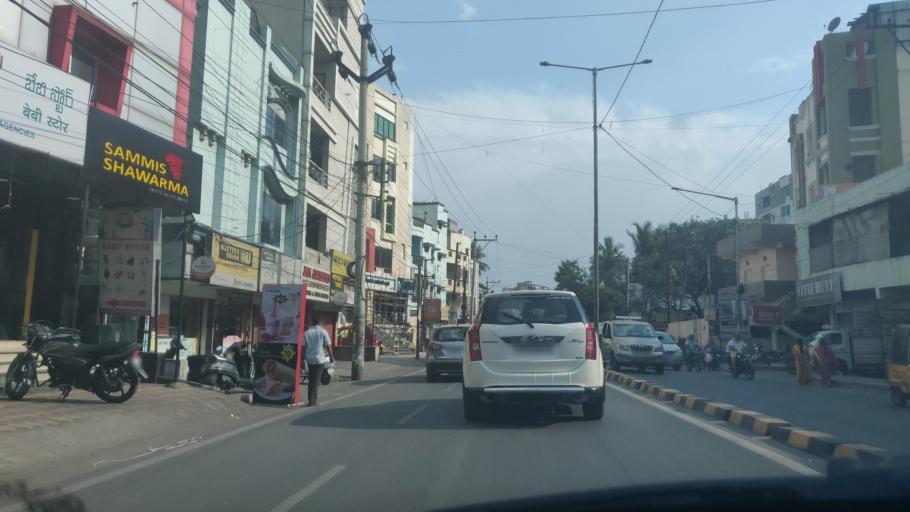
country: IN
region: Telangana
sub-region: Rangareddi
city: Gaddi Annaram
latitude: 17.3935
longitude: 78.5109
